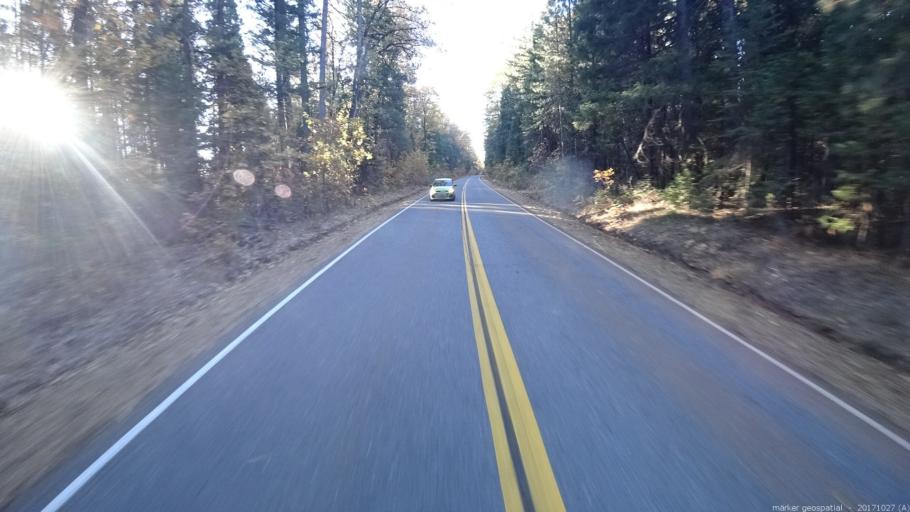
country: US
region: California
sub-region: Shasta County
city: Burney
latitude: 40.9773
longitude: -121.9306
